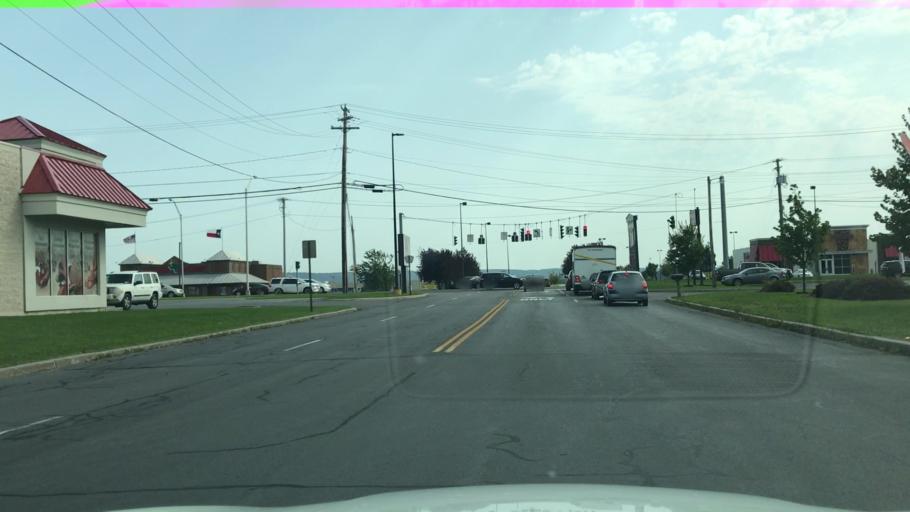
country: US
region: New York
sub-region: Jefferson County
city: Brownville
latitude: 43.9748
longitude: -75.9599
